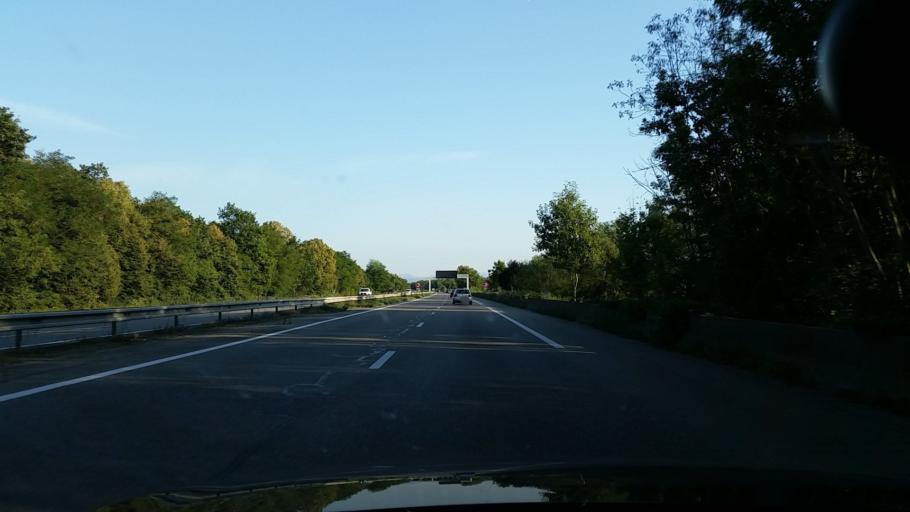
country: FR
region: Alsace
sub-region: Departement du Haut-Rhin
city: Bartenheim
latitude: 47.6309
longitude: 7.5038
